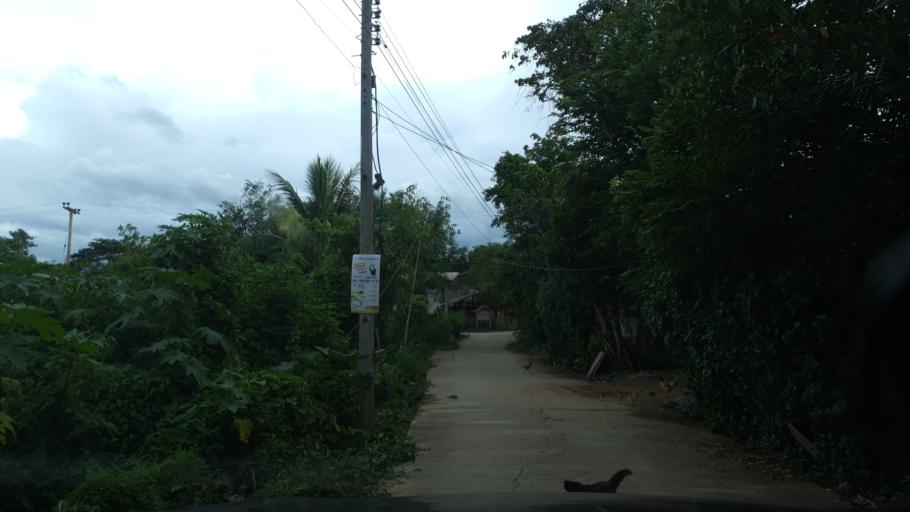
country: TH
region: Chiang Mai
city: Mae On
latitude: 18.6635
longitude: 99.2940
